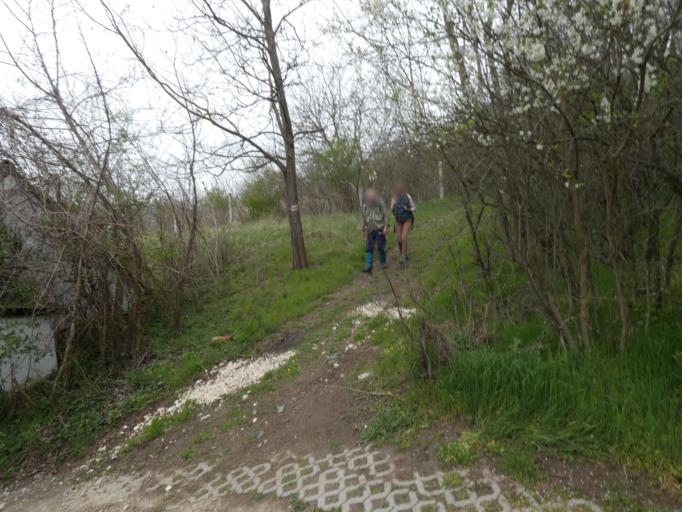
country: HU
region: Fejer
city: Szarliget
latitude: 47.4999
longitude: 18.5666
